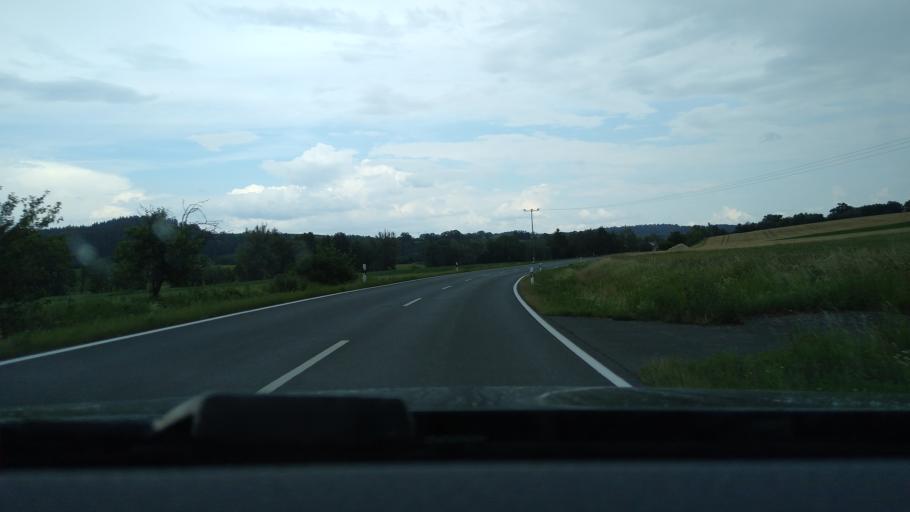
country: DE
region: Bavaria
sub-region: Regierungsbezirk Mittelfranken
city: Trautskirchen
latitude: 49.4623
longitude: 10.5571
